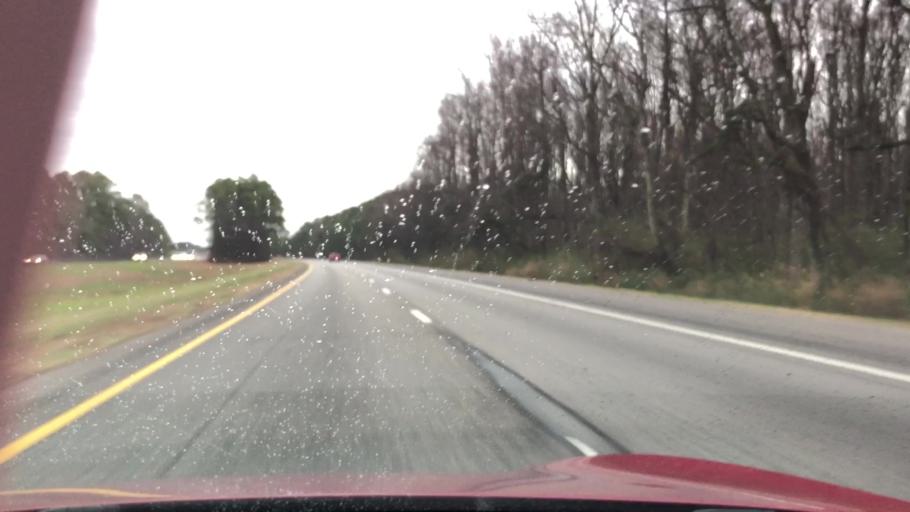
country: US
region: South Carolina
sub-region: Dillon County
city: Latta
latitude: 34.3583
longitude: -79.5070
